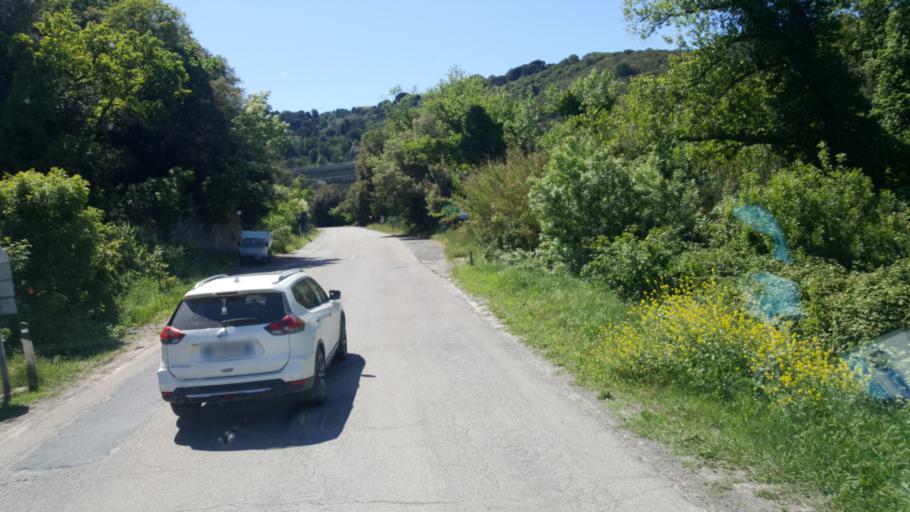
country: IT
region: Tuscany
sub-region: Provincia di Livorno
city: Rosignano Marittimo
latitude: 43.4068
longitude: 10.4941
